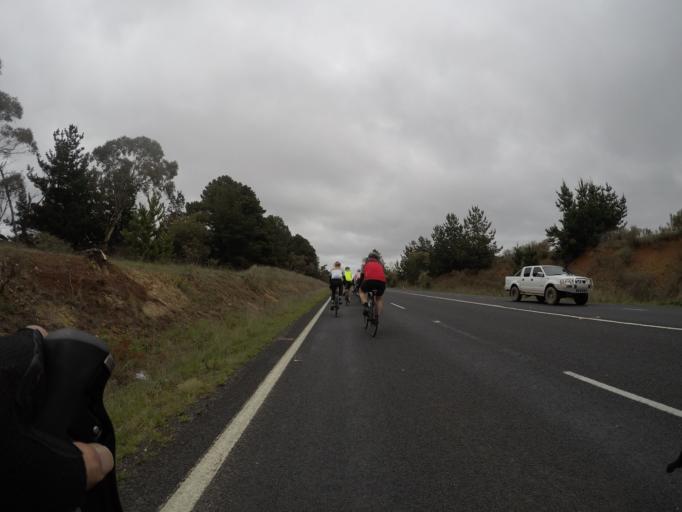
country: AU
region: New South Wales
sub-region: Lithgow
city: Portland
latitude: -33.4332
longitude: 149.8973
